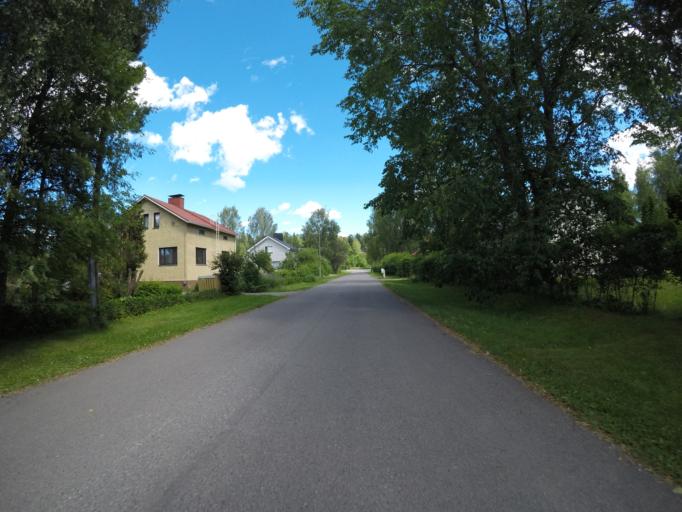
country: FI
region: Haeme
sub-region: Haemeenlinna
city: Haemeenlinna
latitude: 61.0134
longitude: 24.4258
